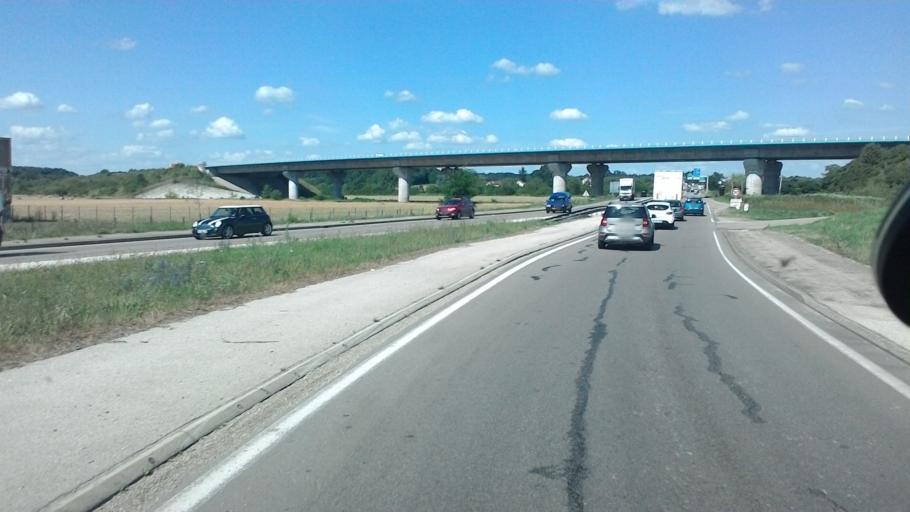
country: FR
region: Franche-Comte
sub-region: Departement du Jura
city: Choisey
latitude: 47.0529
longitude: 5.4367
